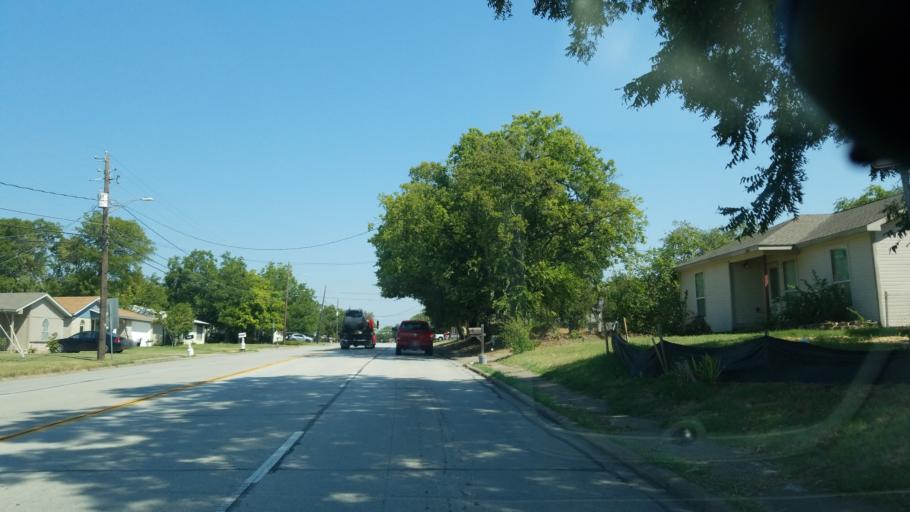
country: US
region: Texas
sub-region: Dallas County
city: Grand Prairie
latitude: 32.7070
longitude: -96.9856
